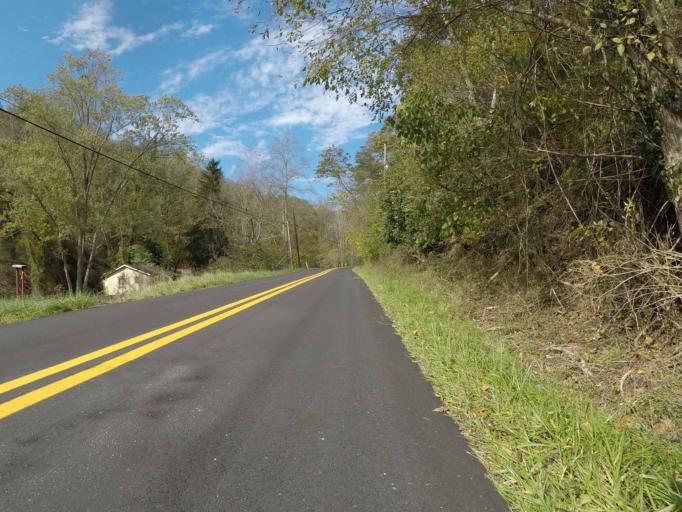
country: US
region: West Virginia
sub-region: Wayne County
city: Lavalette
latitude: 38.3634
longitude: -82.4291
